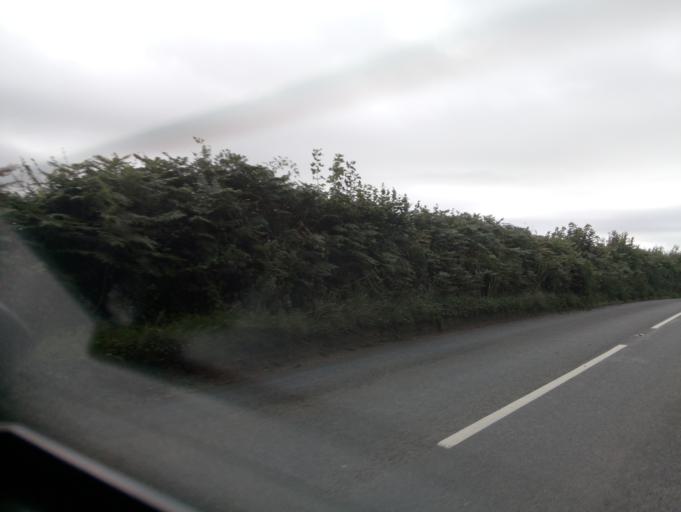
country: GB
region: England
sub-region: Devon
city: Kingsbridge
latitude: 50.2964
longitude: -3.7960
